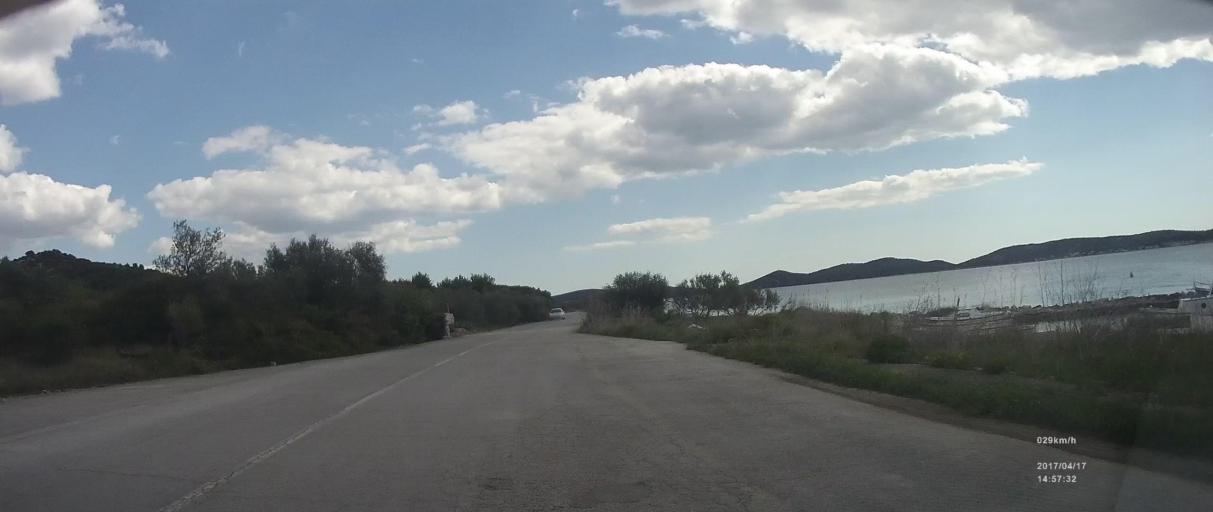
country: HR
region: Sibensko-Kniniska
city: Murter
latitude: 43.8433
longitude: 15.6254
